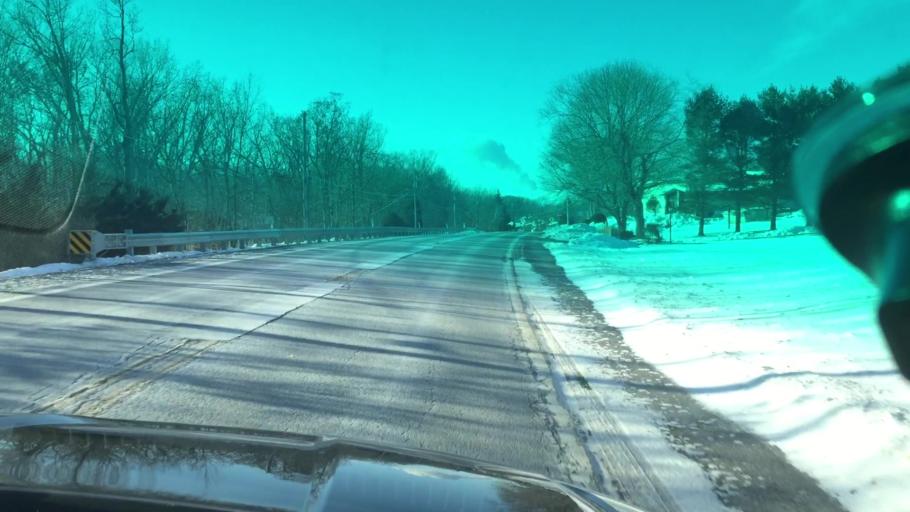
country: US
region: Pennsylvania
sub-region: Luzerne County
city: Freeland
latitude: 41.0155
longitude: -75.9138
